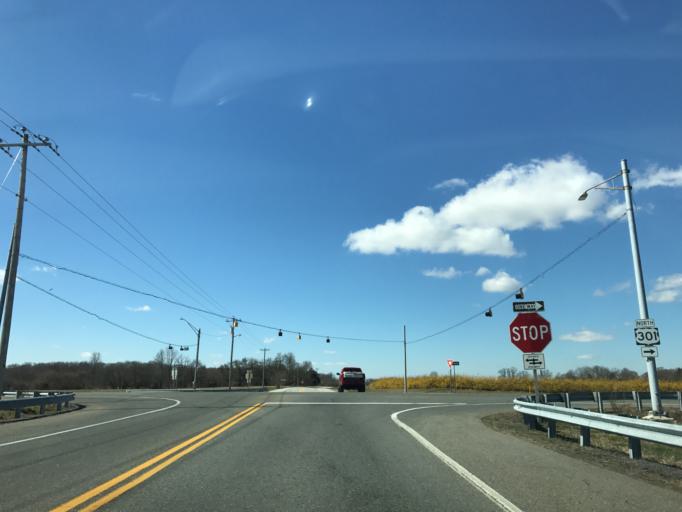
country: US
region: Maryland
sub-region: Queen Anne's County
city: Kingstown
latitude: 39.1228
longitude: -75.9421
